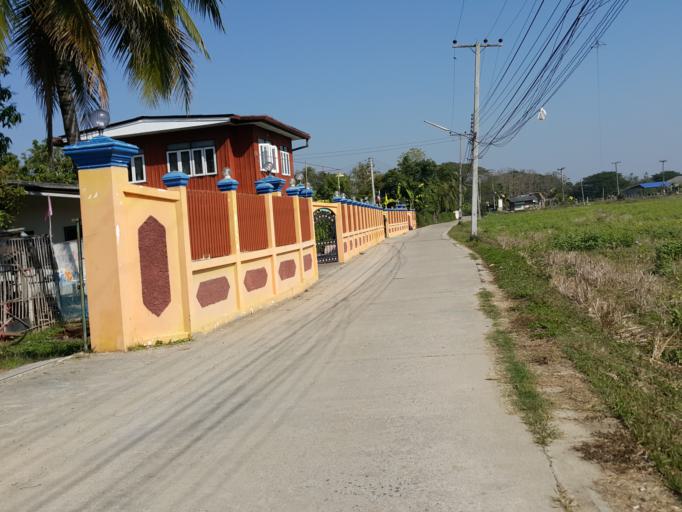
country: TH
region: Chiang Mai
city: San Sai
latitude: 18.8013
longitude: 99.0703
